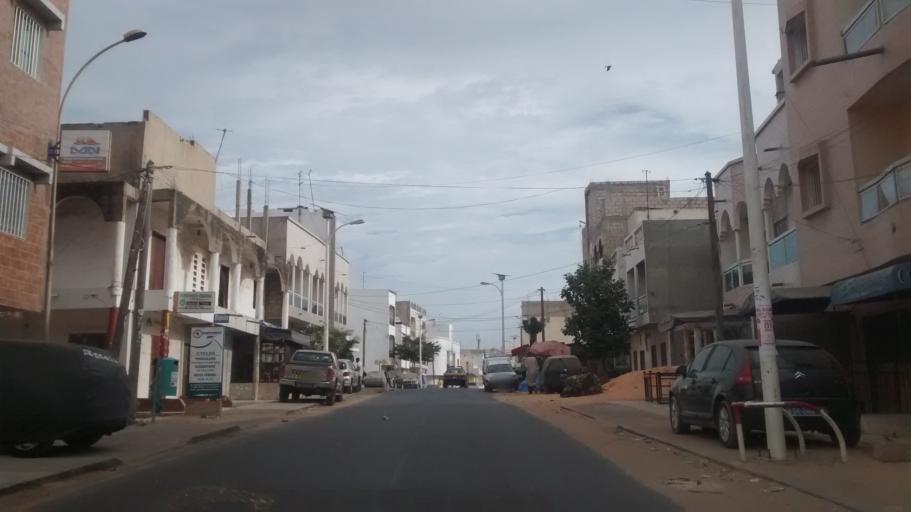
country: SN
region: Dakar
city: Pikine
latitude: 14.7581
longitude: -17.4241
